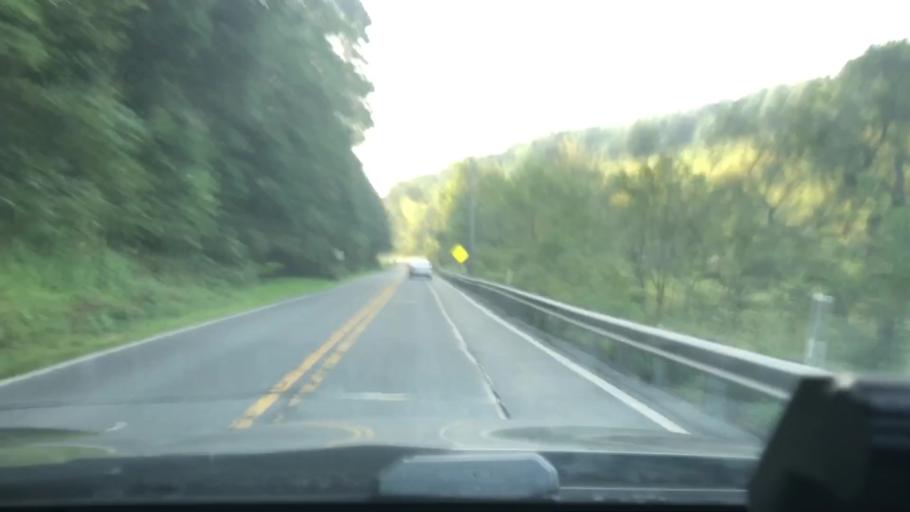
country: US
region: Pennsylvania
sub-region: Berks County
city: Kutztown
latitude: 40.5513
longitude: -75.8019
